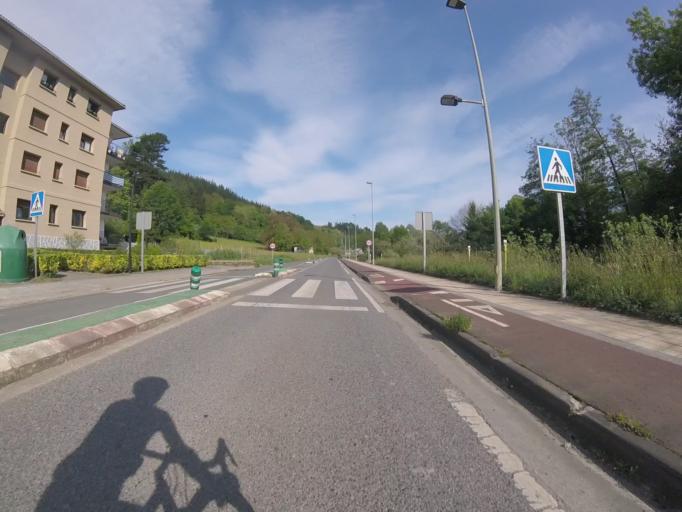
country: ES
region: Basque Country
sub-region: Provincia de Guipuzcoa
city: Ormaiztegui
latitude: 43.0449
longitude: -2.2580
